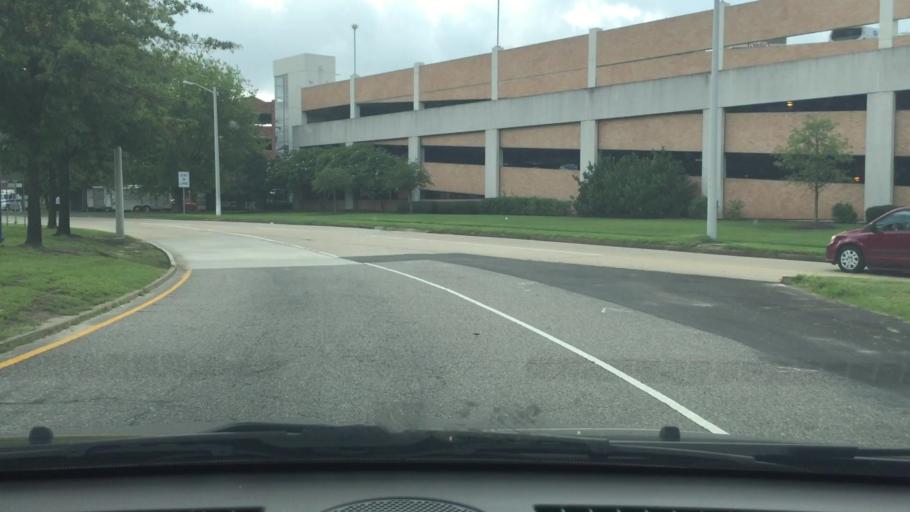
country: US
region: Virginia
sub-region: City of Norfolk
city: Norfolk
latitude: 36.8640
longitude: -76.3038
